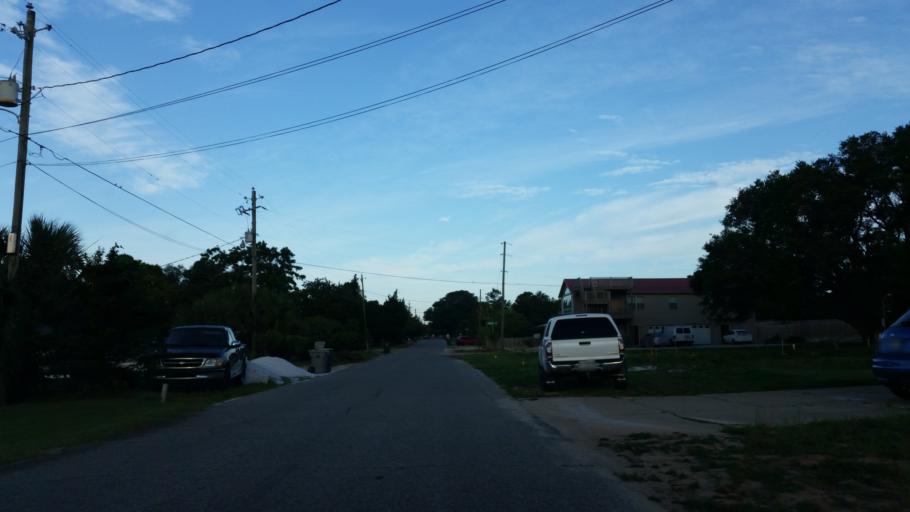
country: US
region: Alabama
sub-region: Baldwin County
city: Orange Beach
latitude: 30.3149
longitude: -87.4325
